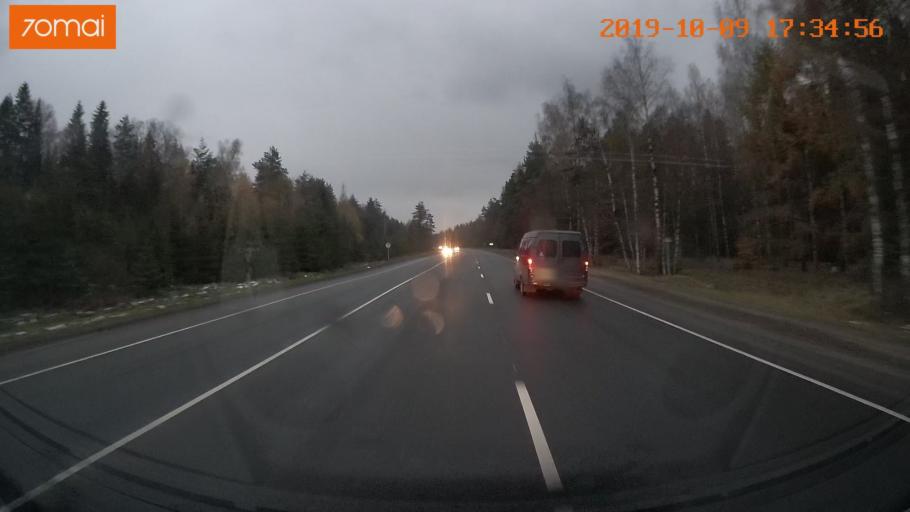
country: RU
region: Ivanovo
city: Bogorodskoye
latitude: 57.1012
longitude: 41.0069
